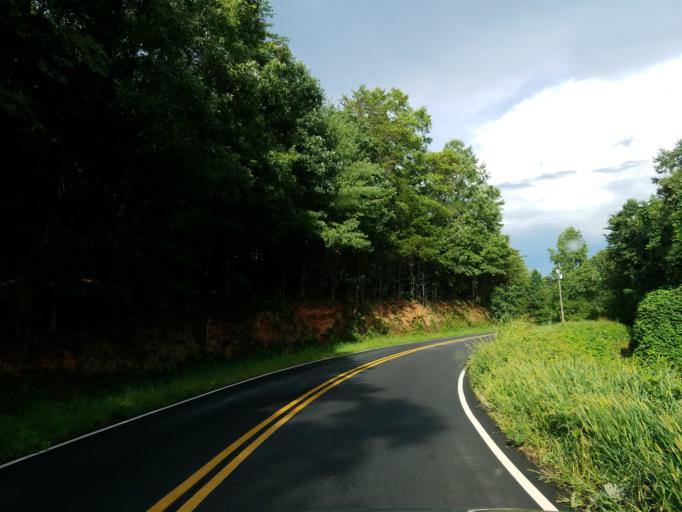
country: US
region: Georgia
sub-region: White County
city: Cleveland
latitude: 34.6365
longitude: -83.8584
